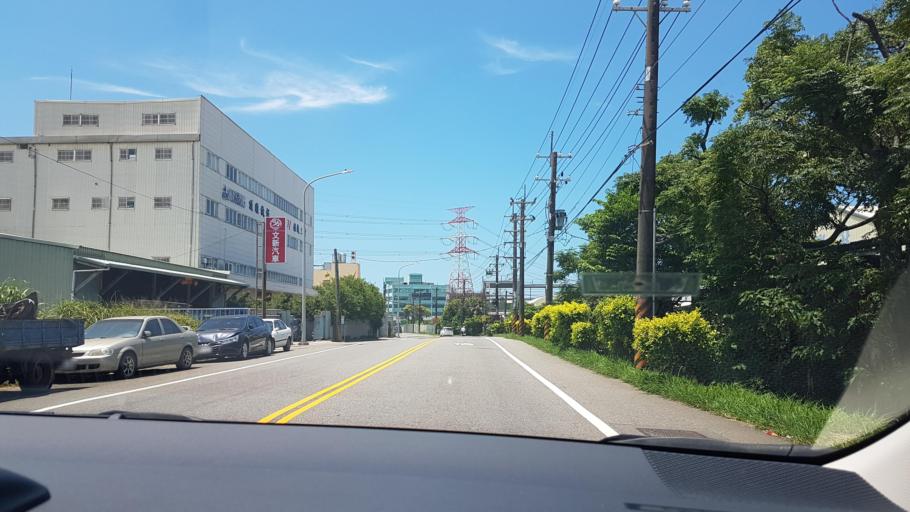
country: TW
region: Taiwan
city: Taoyuan City
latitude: 25.0897
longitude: 121.2766
